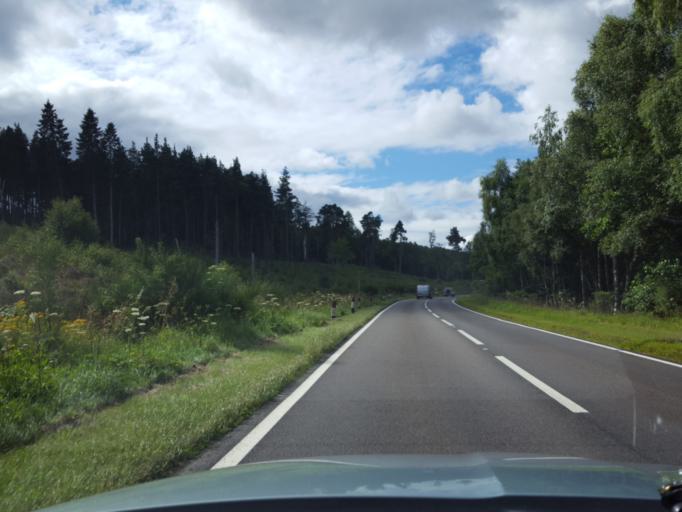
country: GB
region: Scotland
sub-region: Highland
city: Grantown on Spey
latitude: 57.3272
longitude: -3.5518
